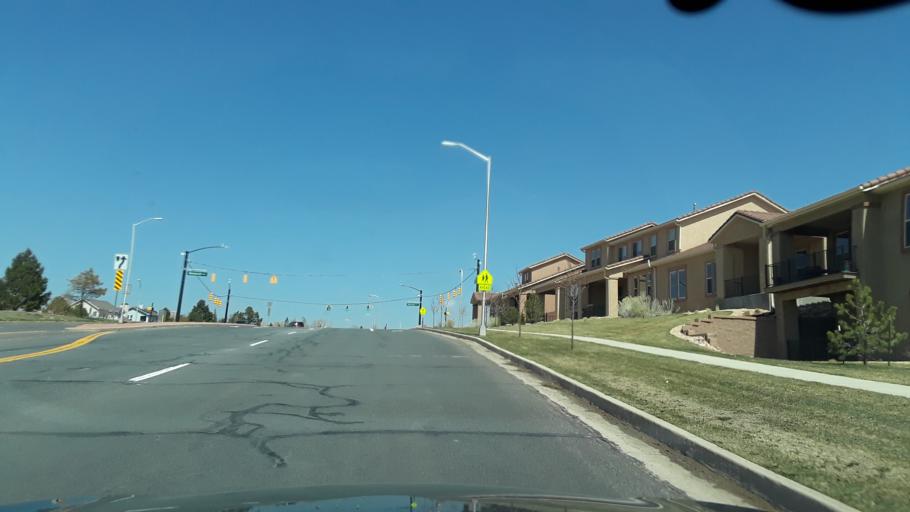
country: US
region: Colorado
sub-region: El Paso County
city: Black Forest
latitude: 38.9534
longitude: -104.7391
